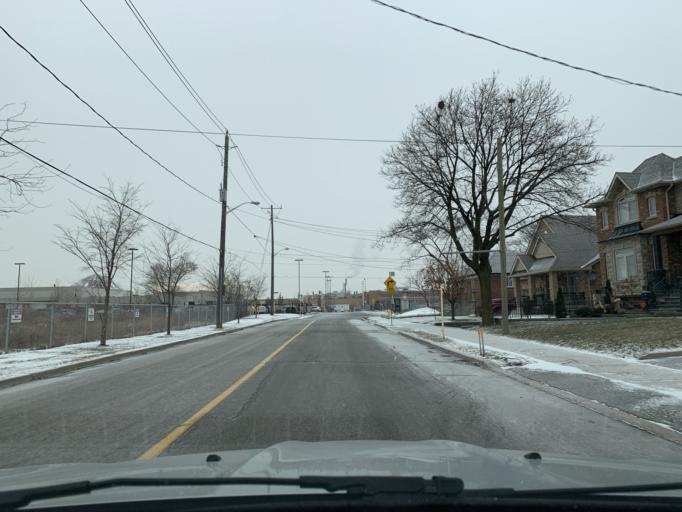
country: CA
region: Ontario
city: Toronto
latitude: 43.7325
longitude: -79.4725
